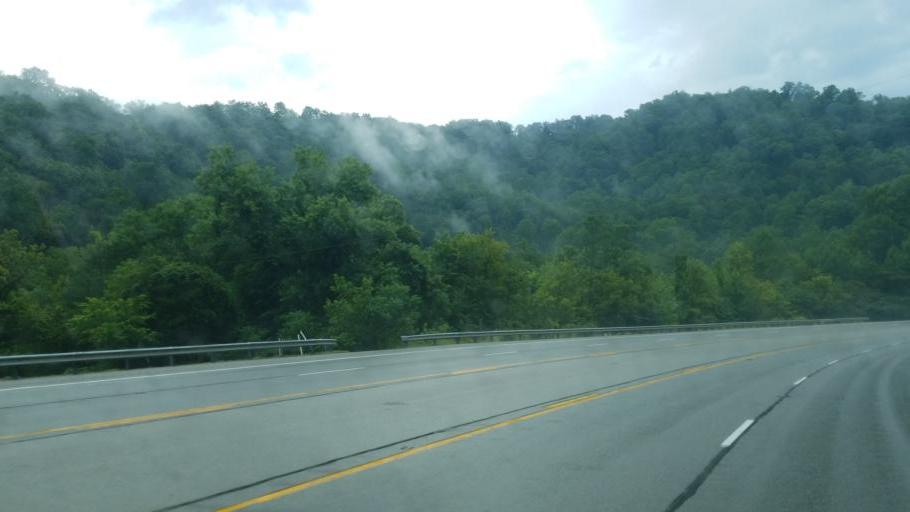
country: US
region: West Virginia
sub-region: Mingo County
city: Williamson
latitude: 37.6435
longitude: -82.2631
